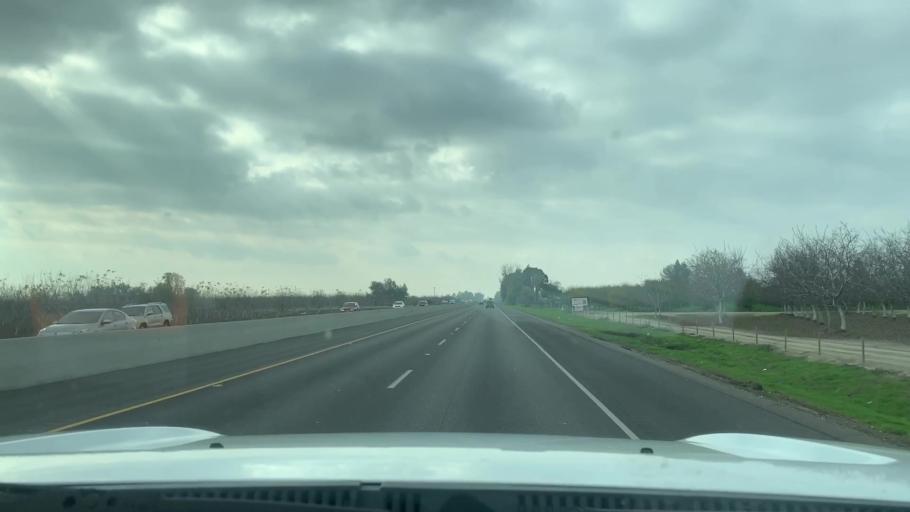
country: US
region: California
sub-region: Kings County
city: Armona
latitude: 36.3060
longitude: -119.7214
